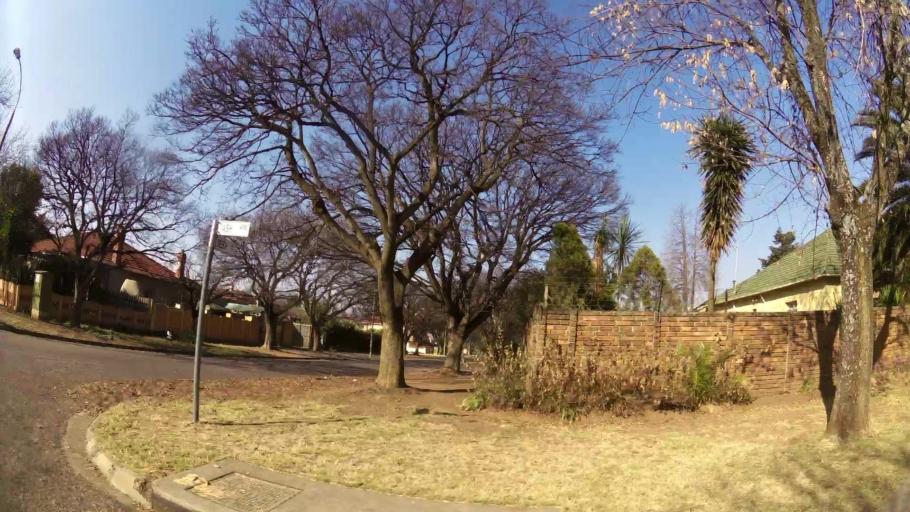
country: ZA
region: Gauteng
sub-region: Ekurhuleni Metropolitan Municipality
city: Boksburg
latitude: -26.2152
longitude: 28.2411
